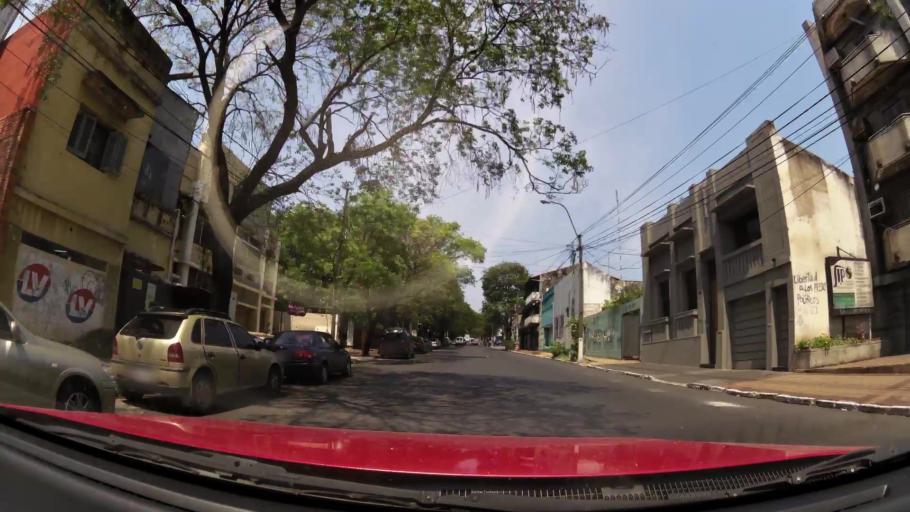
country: PY
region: Asuncion
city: Asuncion
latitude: -25.2844
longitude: -57.6456
